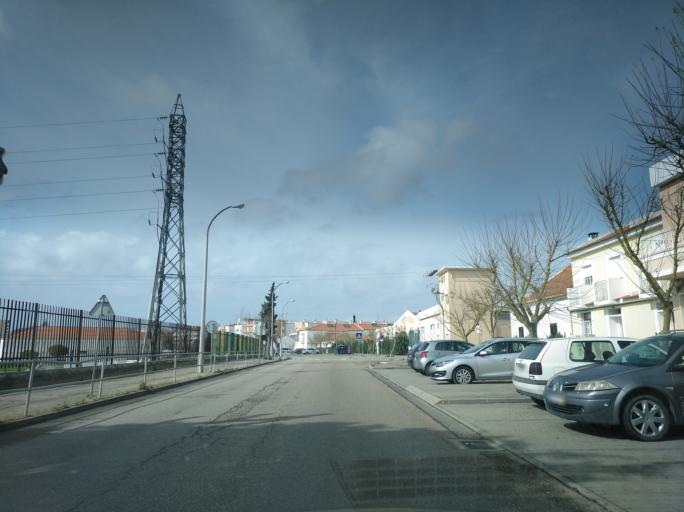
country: PT
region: Setubal
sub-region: Grandola
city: Grandola
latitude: 38.1721
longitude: -8.5587
